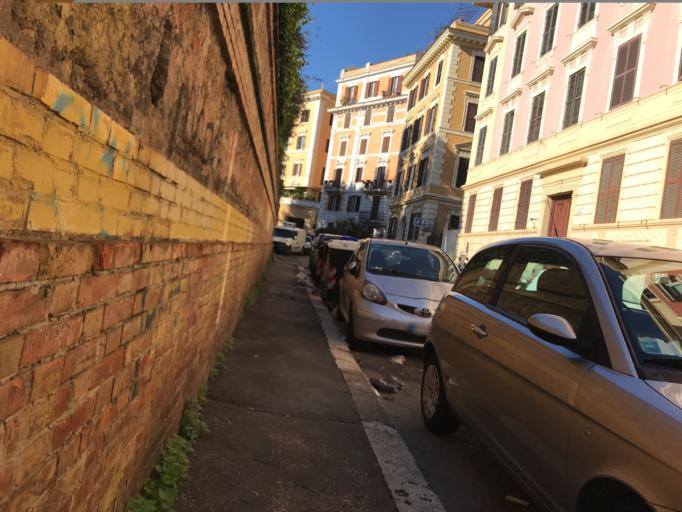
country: IT
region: Latium
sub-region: Citta metropolitana di Roma Capitale
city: Rome
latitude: 41.9164
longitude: 12.5007
